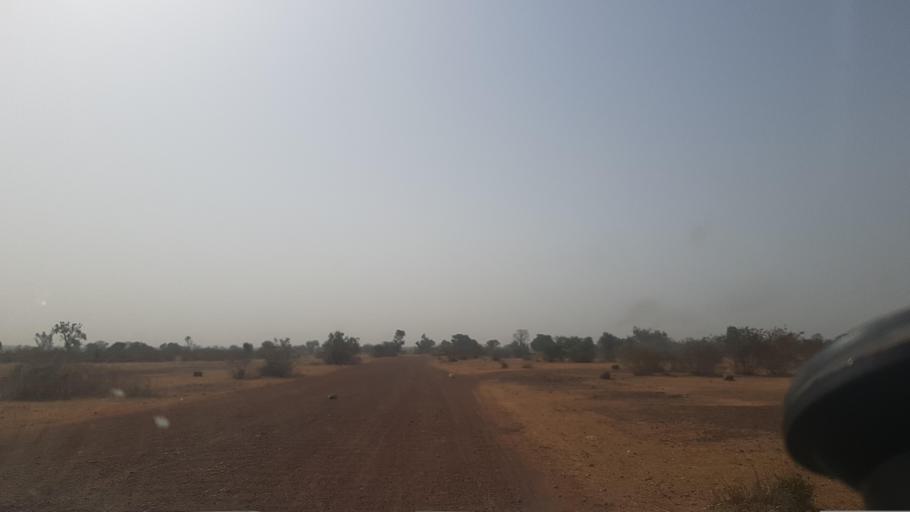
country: ML
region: Segou
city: Baroueli
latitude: 13.1546
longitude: -6.5166
